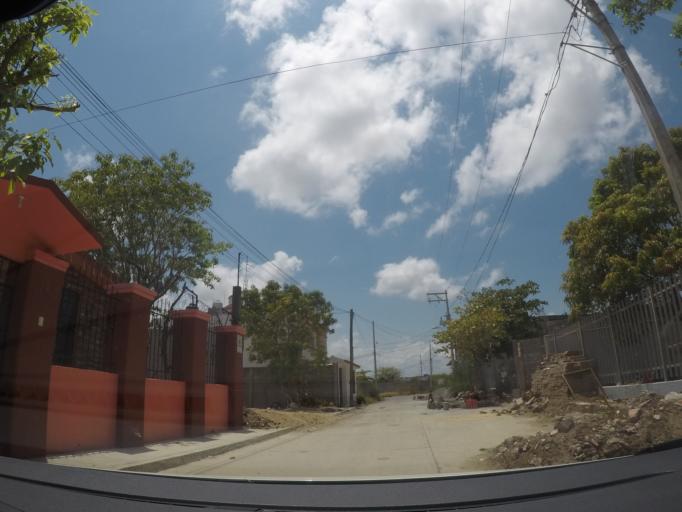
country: MX
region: Oaxaca
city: Juchitan de Zaragoza
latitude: 16.4418
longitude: -95.0103
